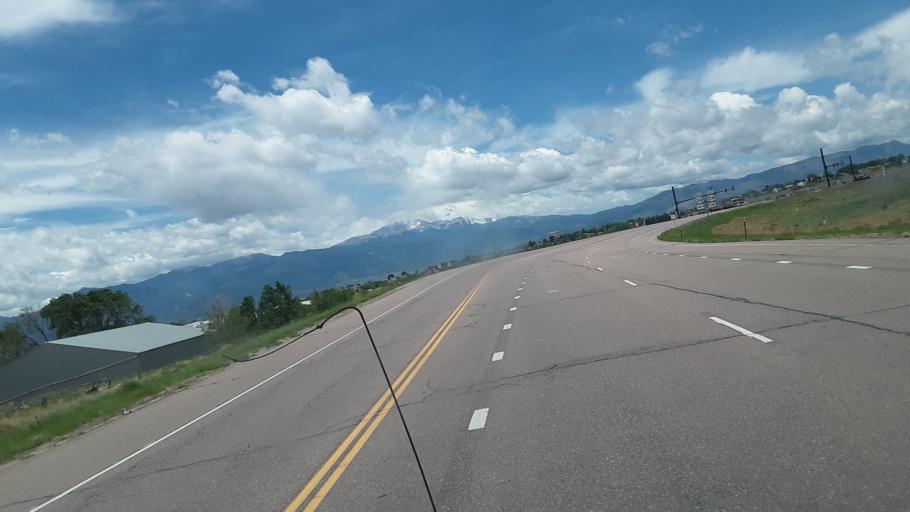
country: US
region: Colorado
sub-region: El Paso County
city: Cimarron Hills
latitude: 38.8420
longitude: -104.6880
